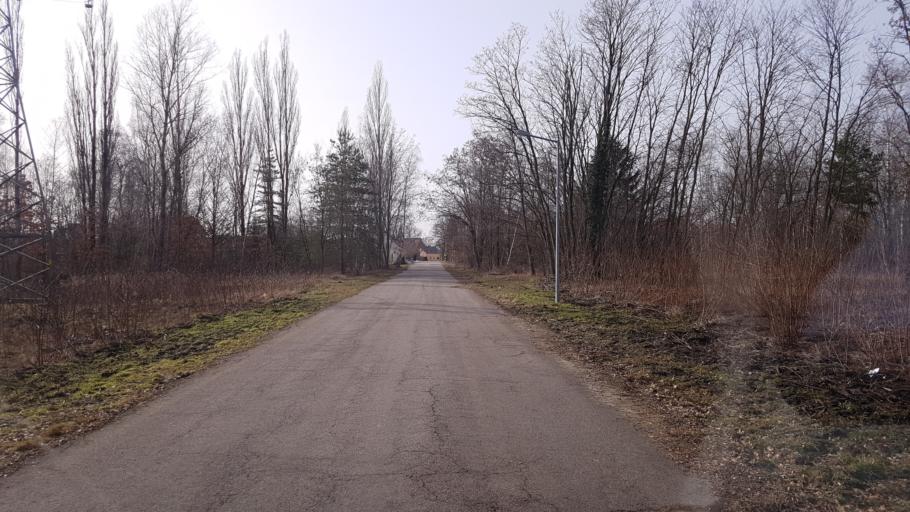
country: DE
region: Brandenburg
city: Schipkau
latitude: 51.5296
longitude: 13.8353
